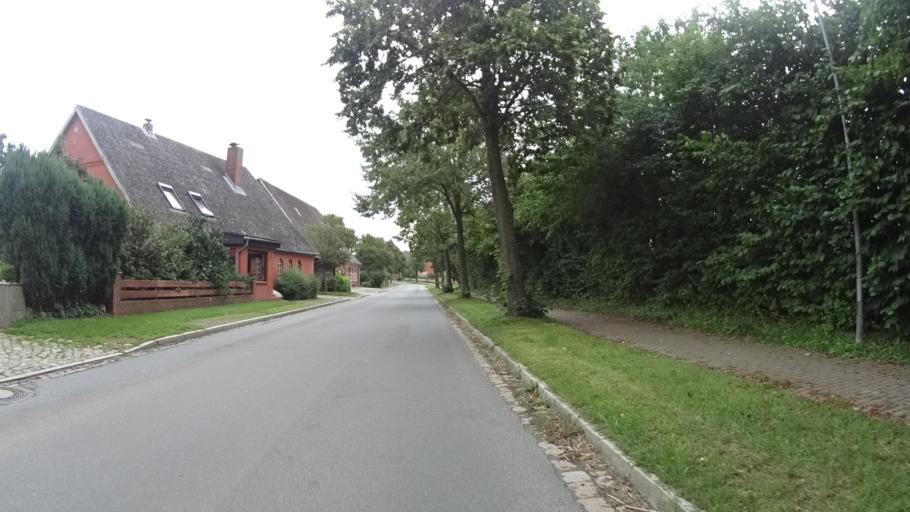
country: DE
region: Schleswig-Holstein
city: Duvensee
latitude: 53.6942
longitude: 10.5683
